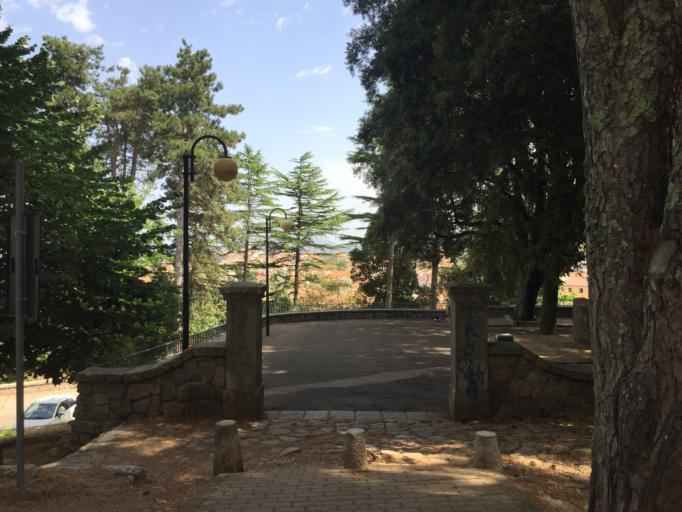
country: IT
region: Sardinia
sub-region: Provincia di Olbia-Tempio
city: Tempio Pausania
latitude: 40.8995
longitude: 9.0981
